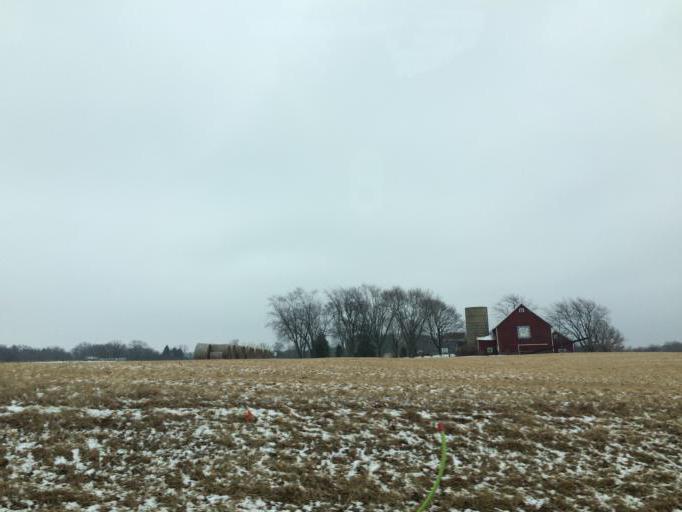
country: US
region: Illinois
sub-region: McHenry County
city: Lakewood
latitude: 42.2366
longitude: -88.4225
